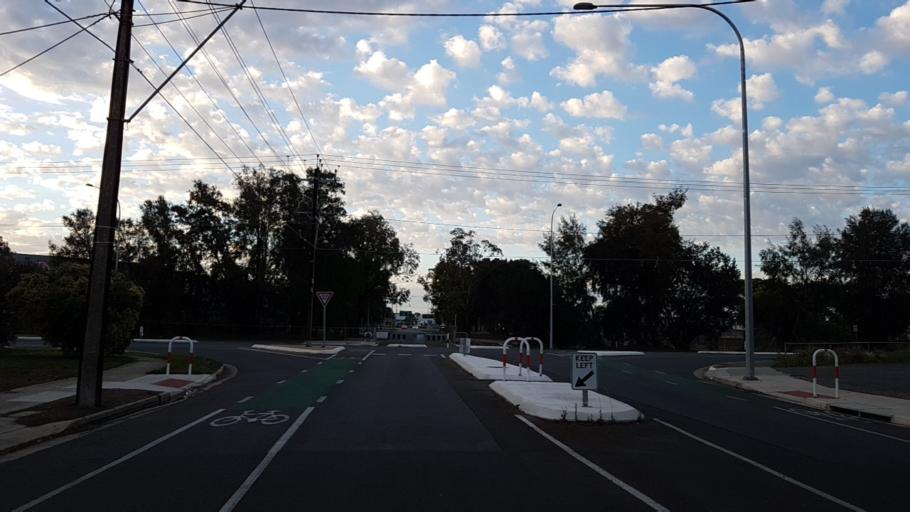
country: AU
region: South Australia
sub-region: City of West Torrens
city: Plympton
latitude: -34.9325
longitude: 138.5346
